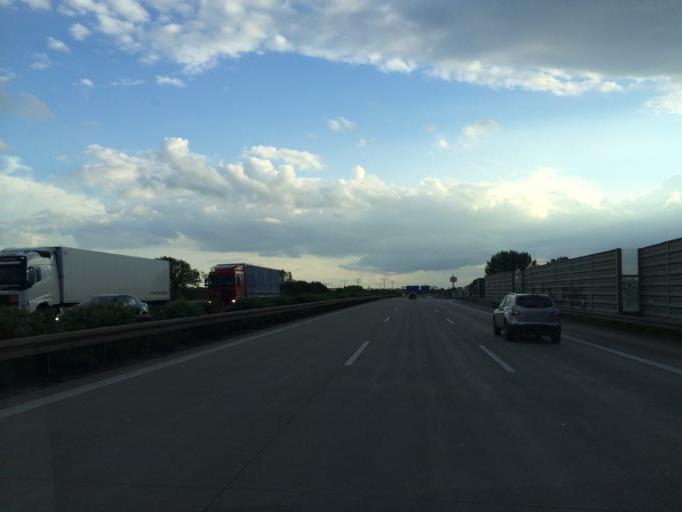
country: DE
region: Saxony-Anhalt
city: Barleben
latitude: 52.1933
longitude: 11.6334
